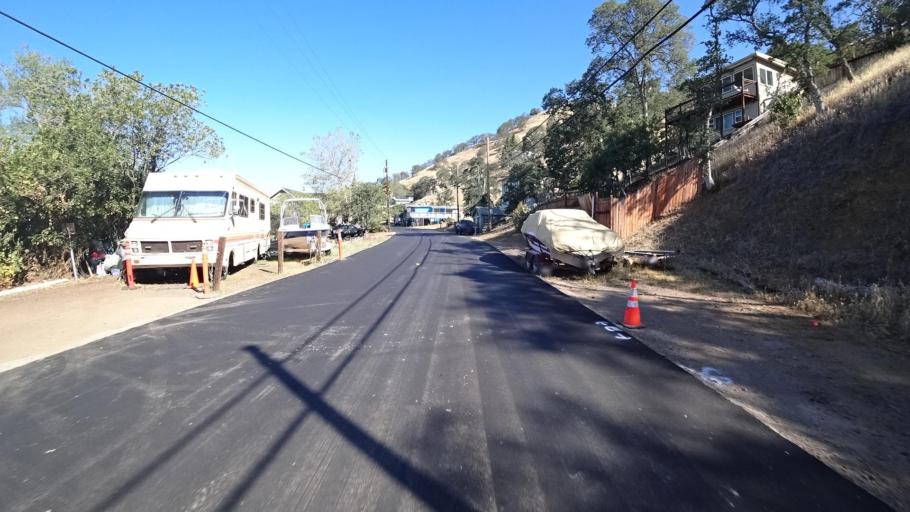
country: US
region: California
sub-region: Lake County
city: Clearlake
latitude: 38.9737
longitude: -122.6740
